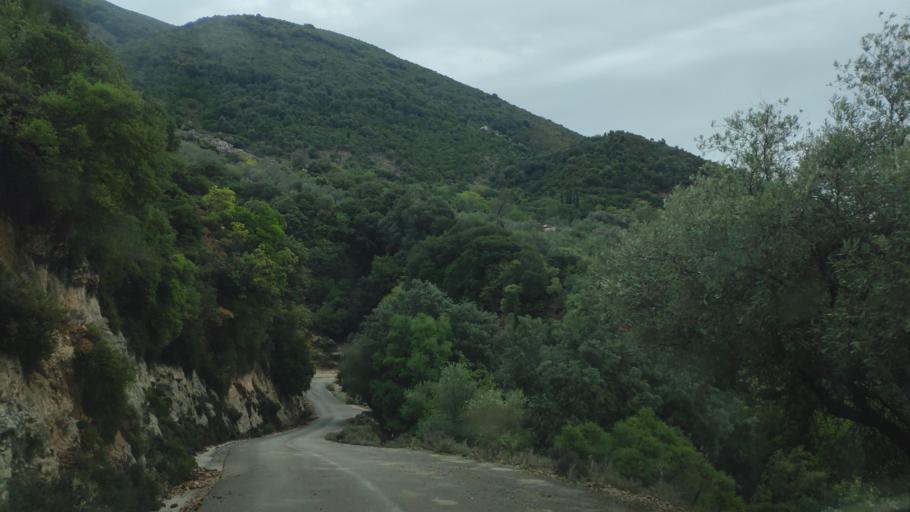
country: GR
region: Epirus
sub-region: Nomos Prevezis
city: Kanalaki
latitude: 39.3465
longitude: 20.6497
